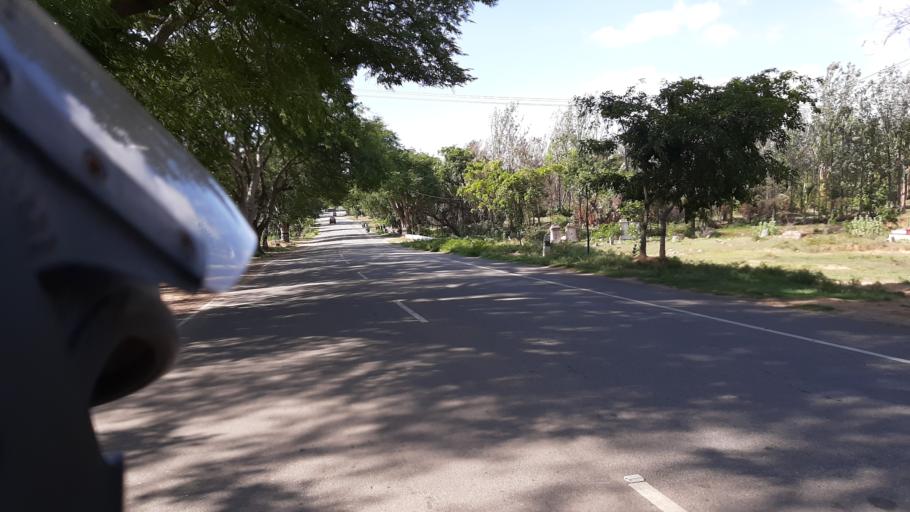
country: IN
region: Tamil Nadu
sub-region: Krishnagiri
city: Denkanikota
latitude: 12.5452
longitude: 77.7874
